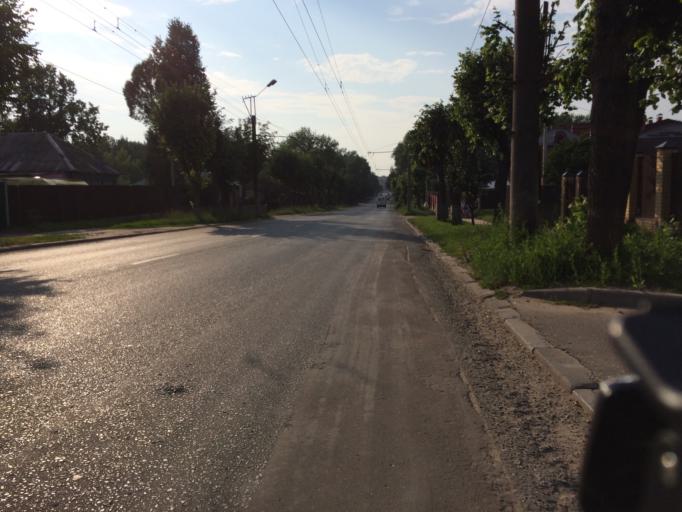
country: RU
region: Mariy-El
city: Yoshkar-Ola
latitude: 56.6324
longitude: 47.9479
